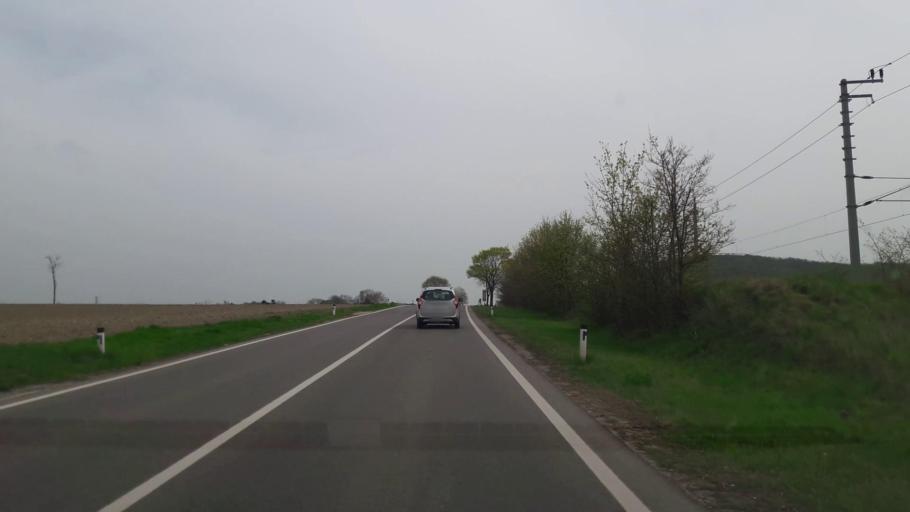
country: AT
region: Lower Austria
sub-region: Politischer Bezirk Bruck an der Leitha
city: Wolfsthal
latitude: 48.1395
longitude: 16.9951
